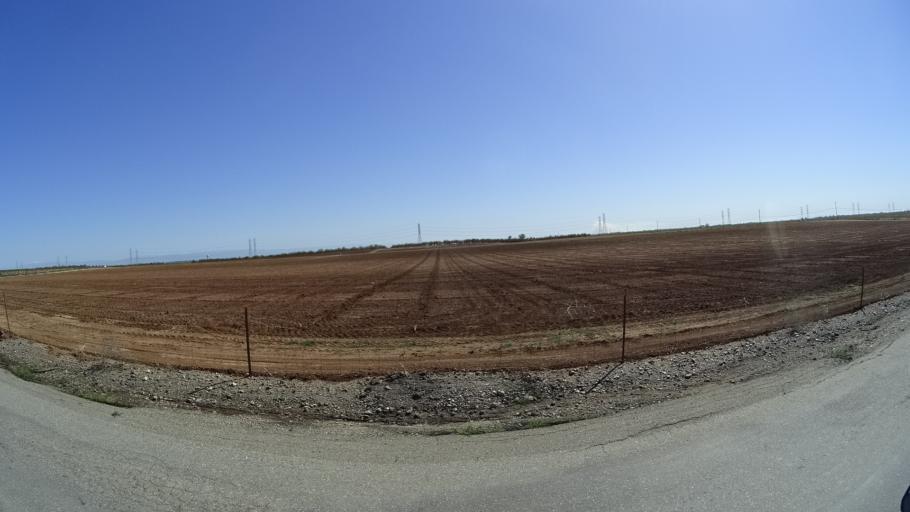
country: US
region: California
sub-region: Glenn County
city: Orland
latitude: 39.6706
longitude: -122.2717
